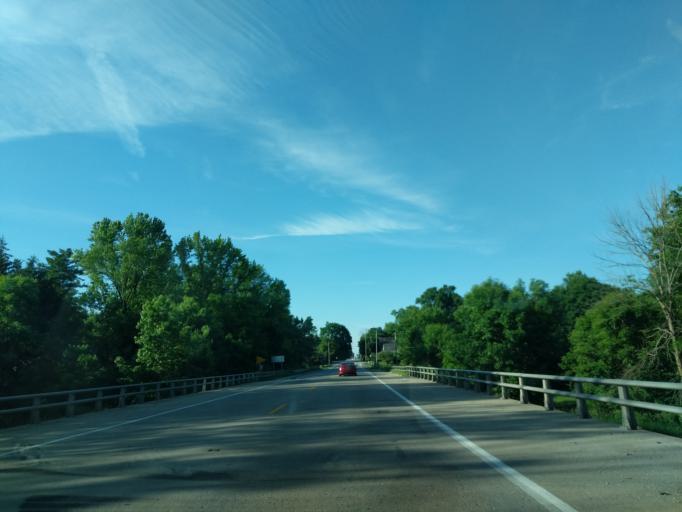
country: US
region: Indiana
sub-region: Madison County
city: Ingalls
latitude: 39.9085
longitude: -85.7708
